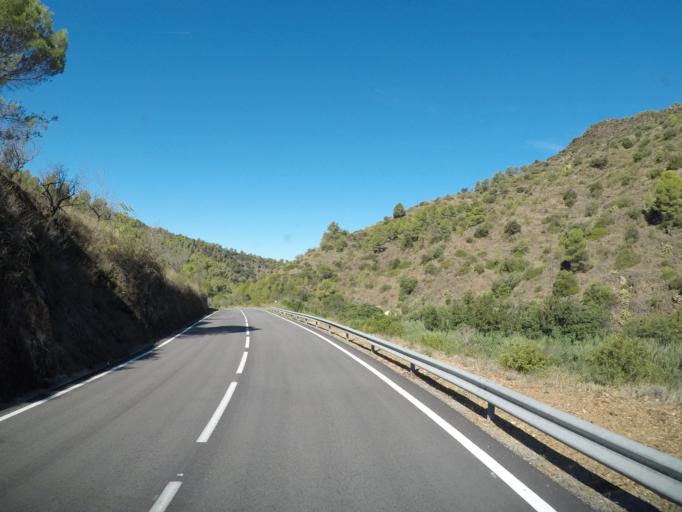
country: ES
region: Catalonia
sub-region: Provincia de Tarragona
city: Falset
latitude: 41.1698
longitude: 0.8046
